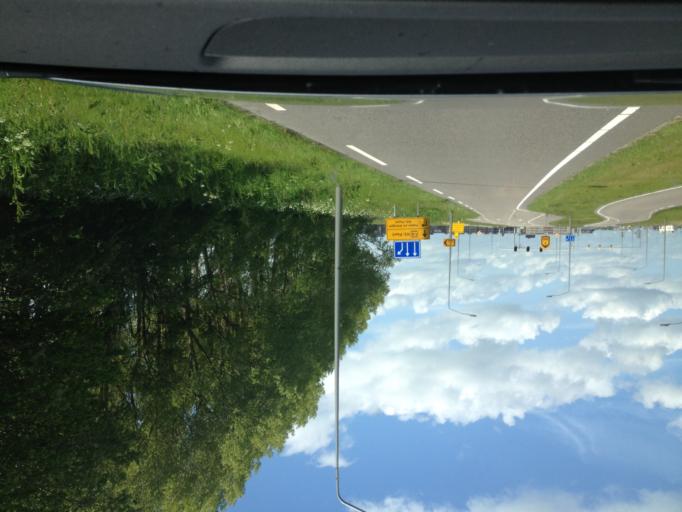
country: NL
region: North Holland
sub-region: Gemeente Naarden
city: Naarden
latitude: 52.3375
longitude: 5.1494
